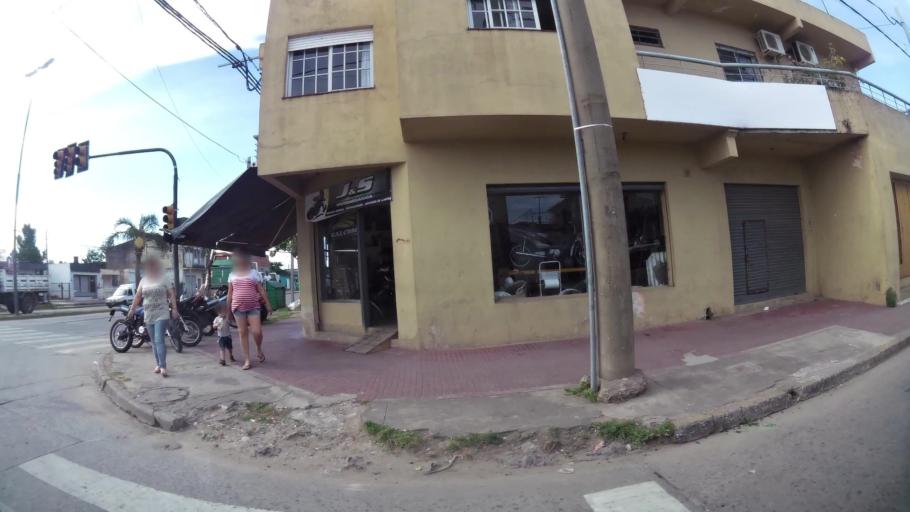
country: AR
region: Santa Fe
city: Granadero Baigorria
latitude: -32.9161
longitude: -60.7136
